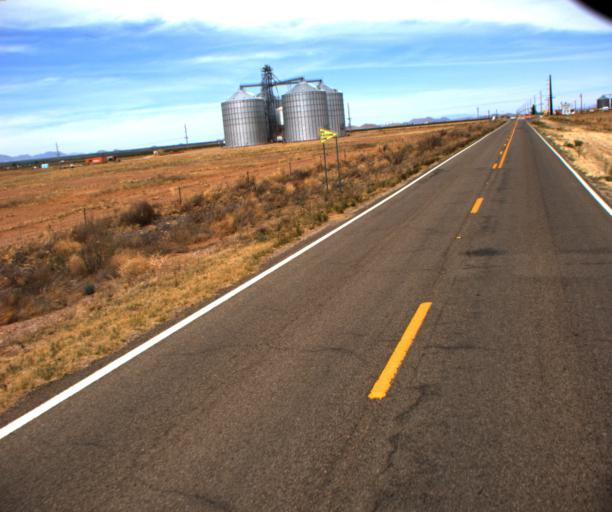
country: US
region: Arizona
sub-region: Cochise County
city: Tombstone
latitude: 31.7556
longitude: -109.6892
